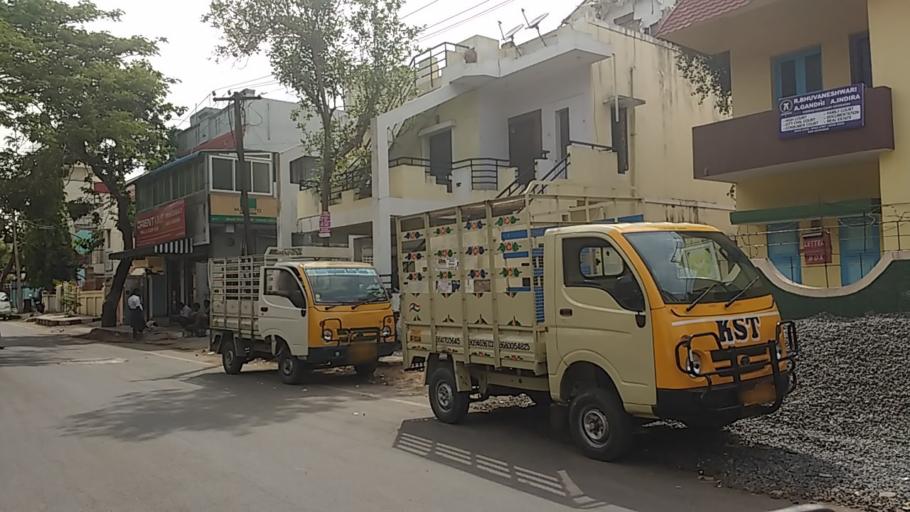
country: IN
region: Tamil Nadu
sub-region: Chennai
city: Chetput
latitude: 13.0516
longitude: 80.2199
